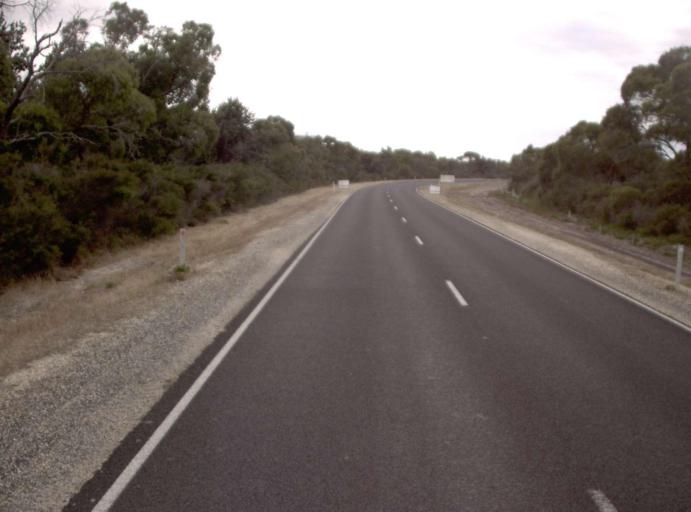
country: AU
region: Victoria
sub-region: East Gippsland
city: Bairnsdale
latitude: -38.1253
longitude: 147.4336
